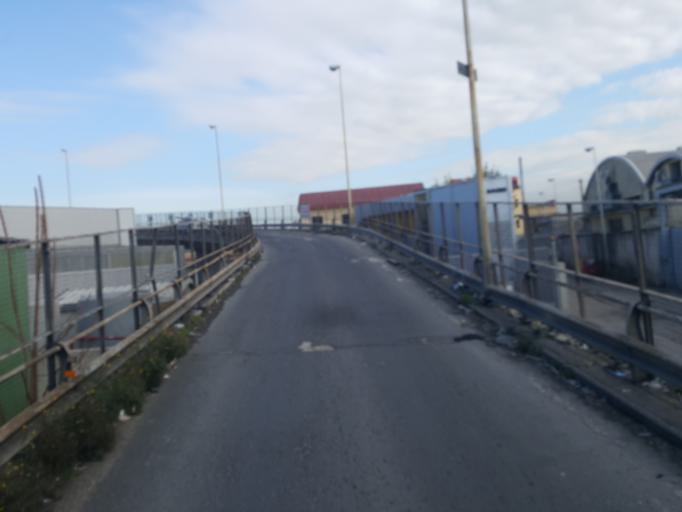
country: IT
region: Campania
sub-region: Provincia di Napoli
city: San Giorgio a Cremano
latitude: 40.8457
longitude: 14.3038
